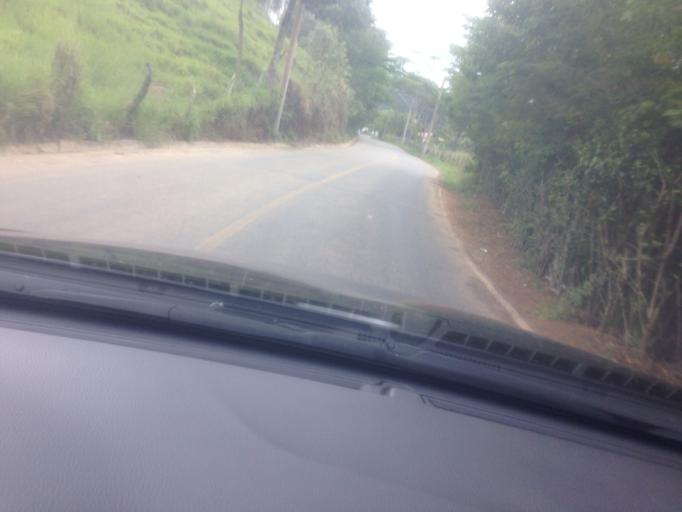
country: BR
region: Espirito Santo
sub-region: Guarapari
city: Guarapari
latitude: -20.5848
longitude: -40.5397
